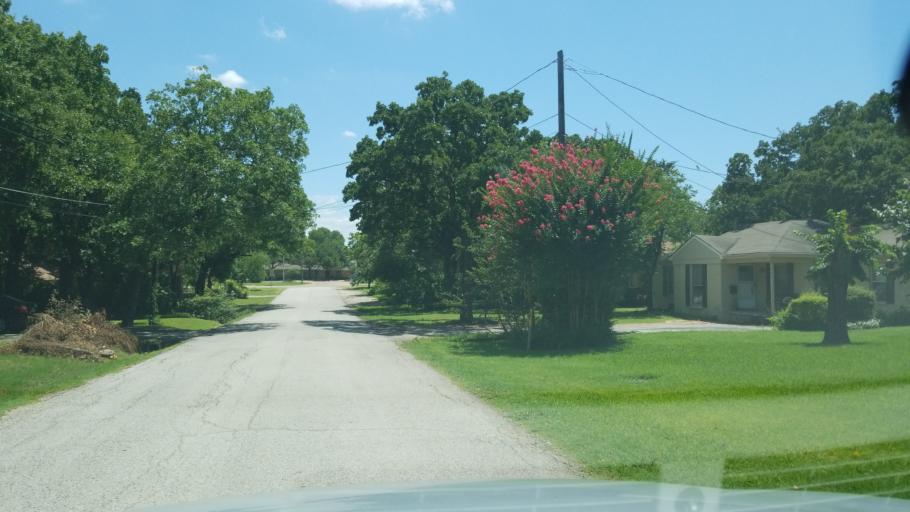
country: US
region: Texas
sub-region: Dallas County
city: Irving
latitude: 32.8109
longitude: -96.9185
